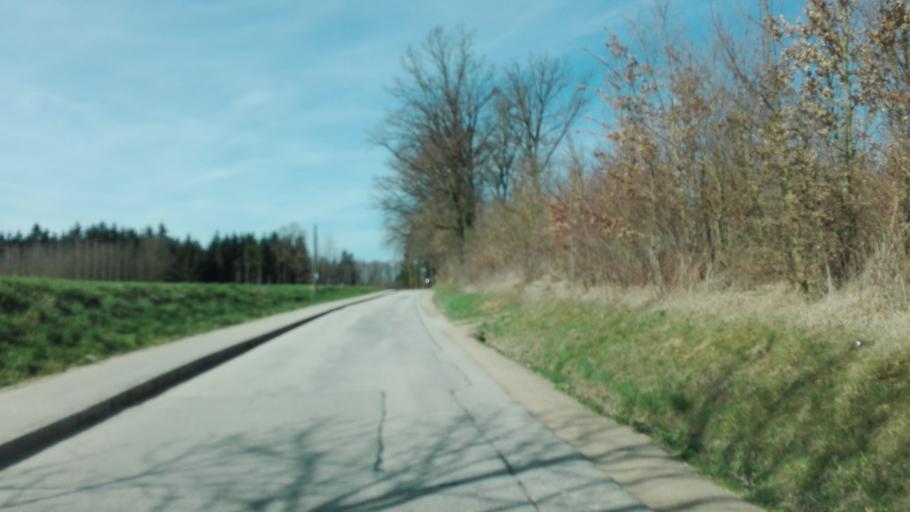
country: AT
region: Lower Austria
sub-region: Politischer Bezirk Amstetten
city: Ennsdorf
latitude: 48.2495
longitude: 14.5206
